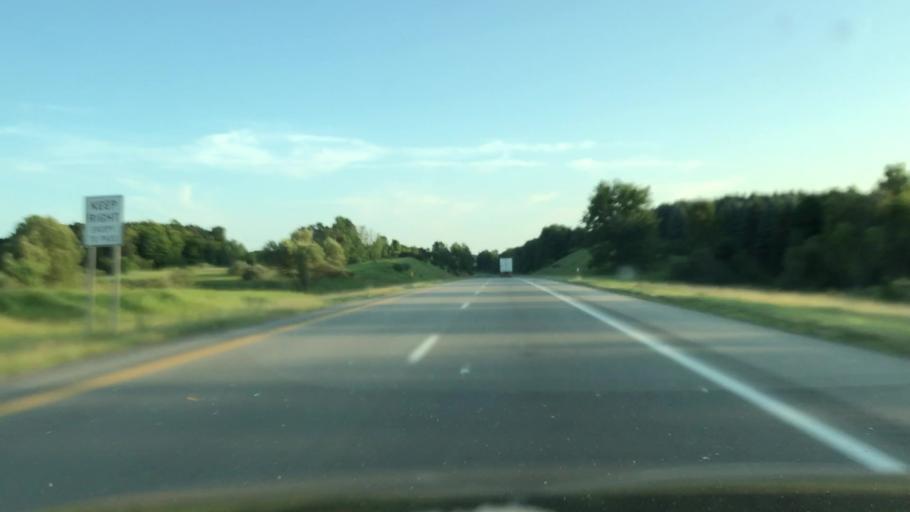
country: US
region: Michigan
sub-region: Osceola County
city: Reed City
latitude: 43.8715
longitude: -85.5318
